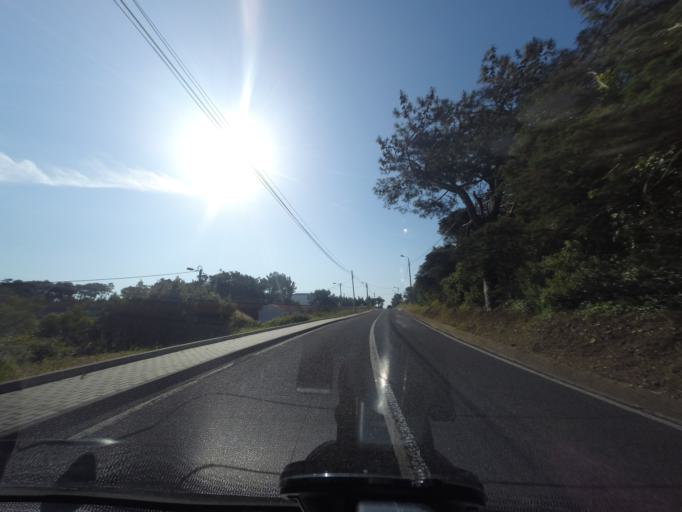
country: PT
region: Lisbon
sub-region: Cascais
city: Alcabideche
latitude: 38.7512
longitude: -9.4383
